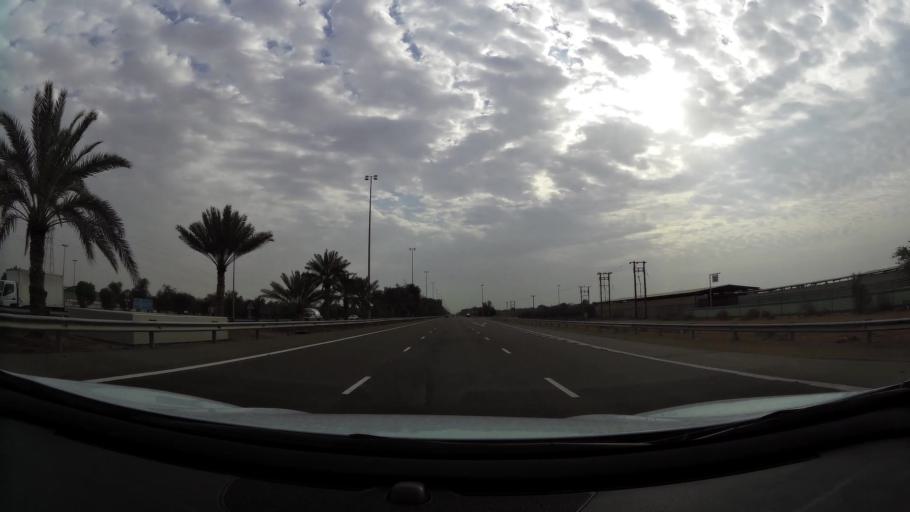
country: AE
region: Abu Dhabi
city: Al Ain
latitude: 24.2040
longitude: 55.3951
